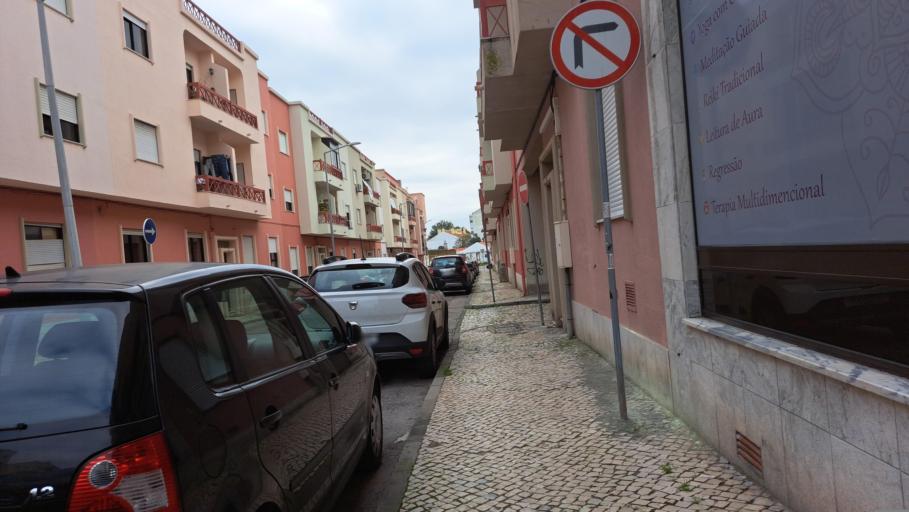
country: PT
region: Setubal
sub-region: Moita
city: Alhos Vedros
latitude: 38.6581
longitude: -9.0476
